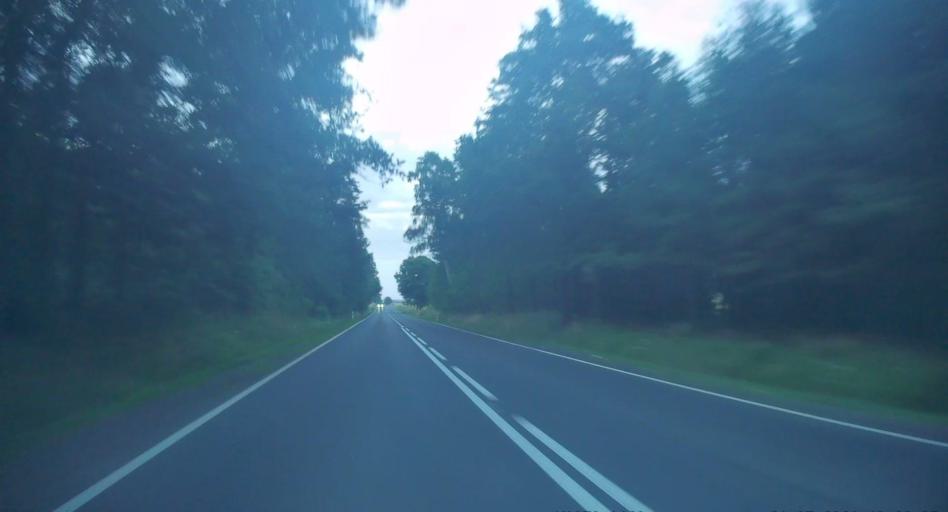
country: PL
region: Opole Voivodeship
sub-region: Powiat oleski
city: Dalachow
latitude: 51.1011
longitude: 18.6074
